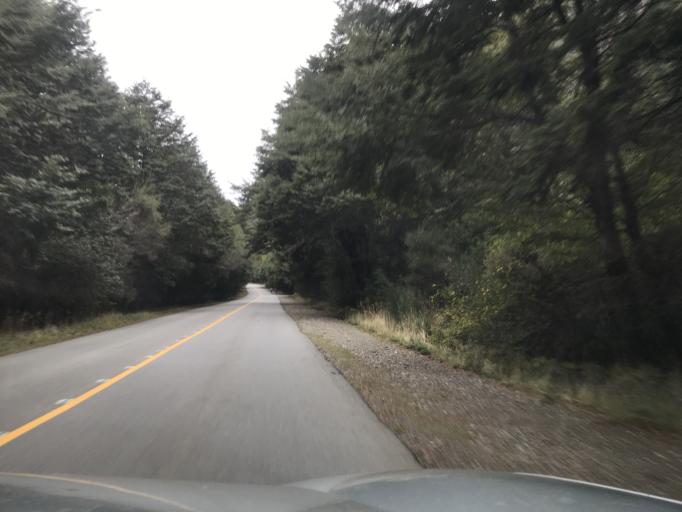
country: AR
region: Rio Negro
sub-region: Departamento de Bariloche
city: San Carlos de Bariloche
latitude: -41.0763
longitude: -71.5656
